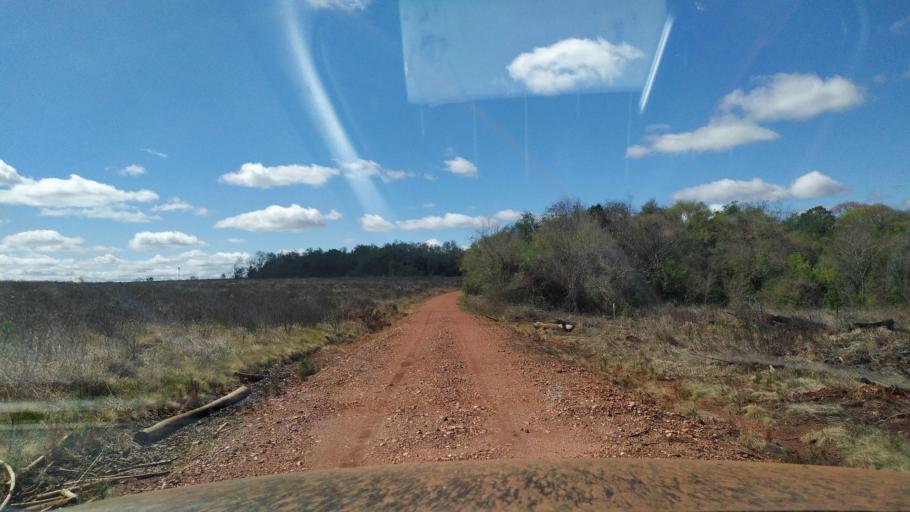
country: AR
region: Corrientes
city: Gobernador Ingeniero Valentin Virasoro
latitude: -28.2909
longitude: -56.0511
